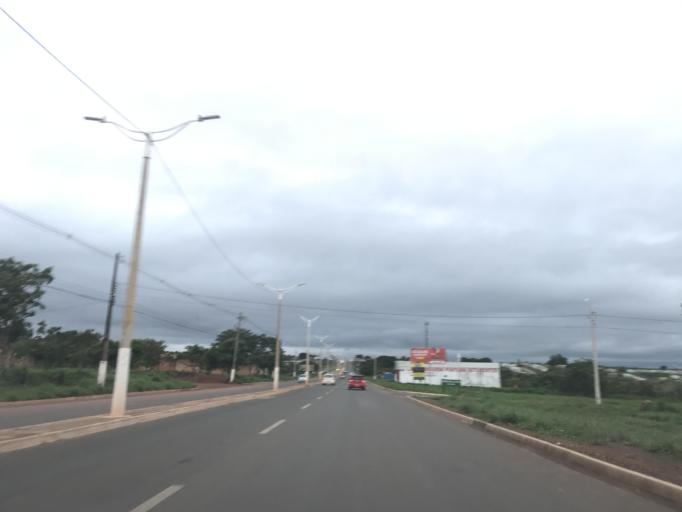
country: BR
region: Goias
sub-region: Luziania
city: Luziania
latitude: -16.2221
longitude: -47.9352
